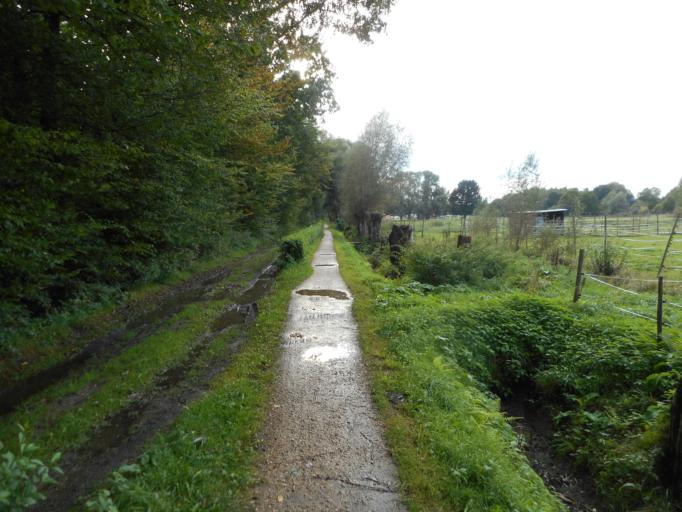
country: BE
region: Flanders
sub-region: Provincie Antwerpen
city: Hemiksem
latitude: 51.1564
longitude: 4.3537
